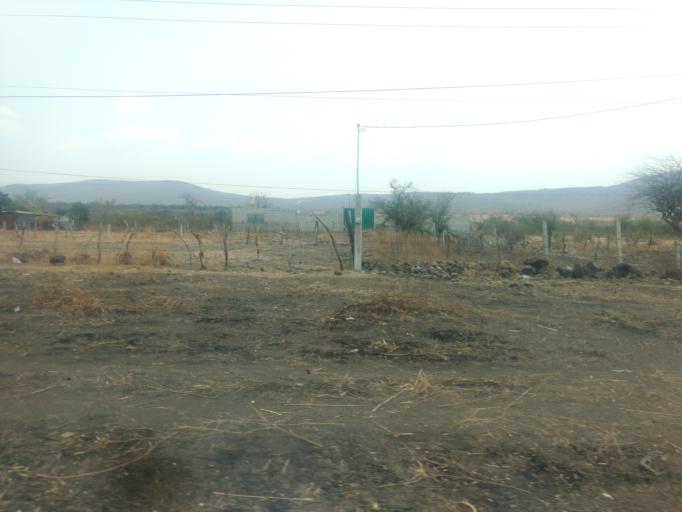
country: MX
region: Morelos
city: La Joya
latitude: 18.6690
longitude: -99.4279
